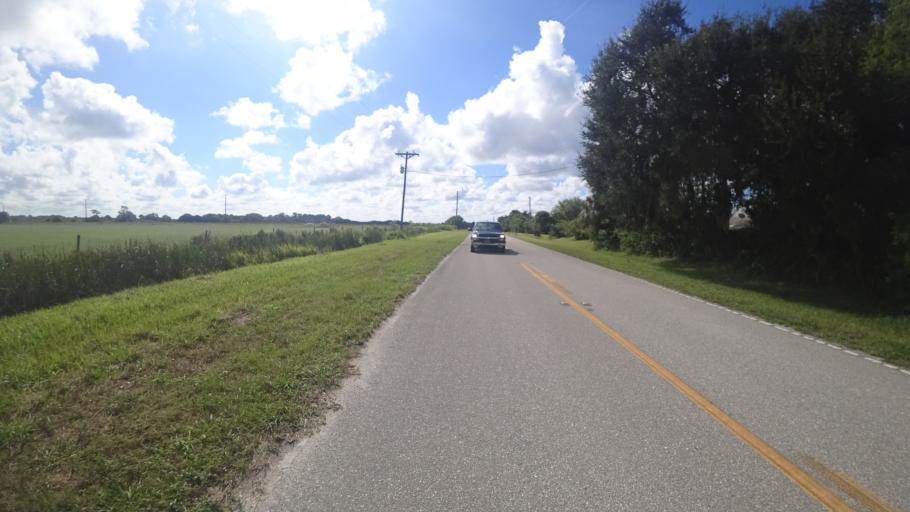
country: US
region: Florida
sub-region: Manatee County
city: Ellenton
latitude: 27.6168
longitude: -82.4818
